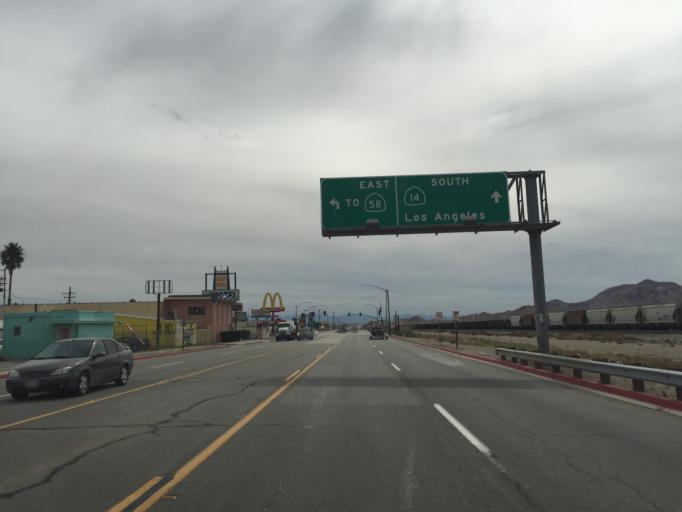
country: US
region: California
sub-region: Kern County
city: Mojave
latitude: 35.0497
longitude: -118.1728
